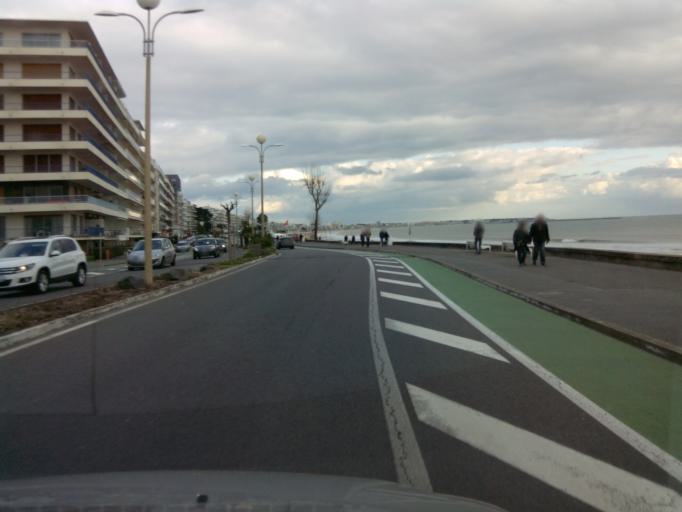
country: FR
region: Pays de la Loire
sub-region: Departement de la Loire-Atlantique
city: La Baule-Escoublac
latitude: 47.2815
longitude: -2.3894
